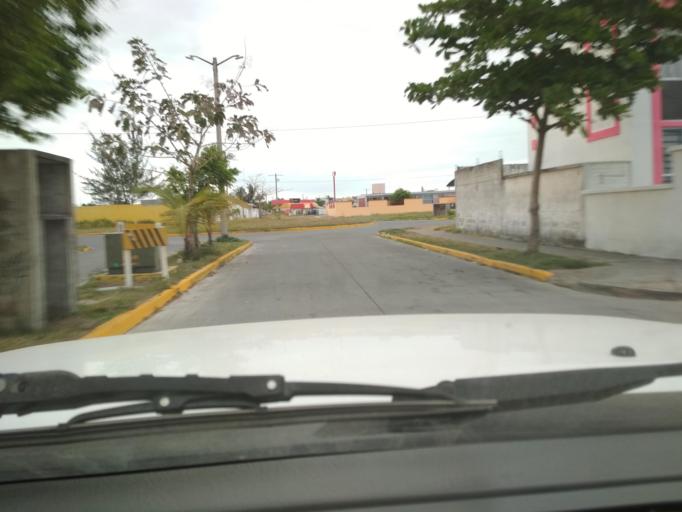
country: MX
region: Veracruz
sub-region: Medellin
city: Fraccionamiento Arboledas San Ramon
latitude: 19.0944
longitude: -96.1599
